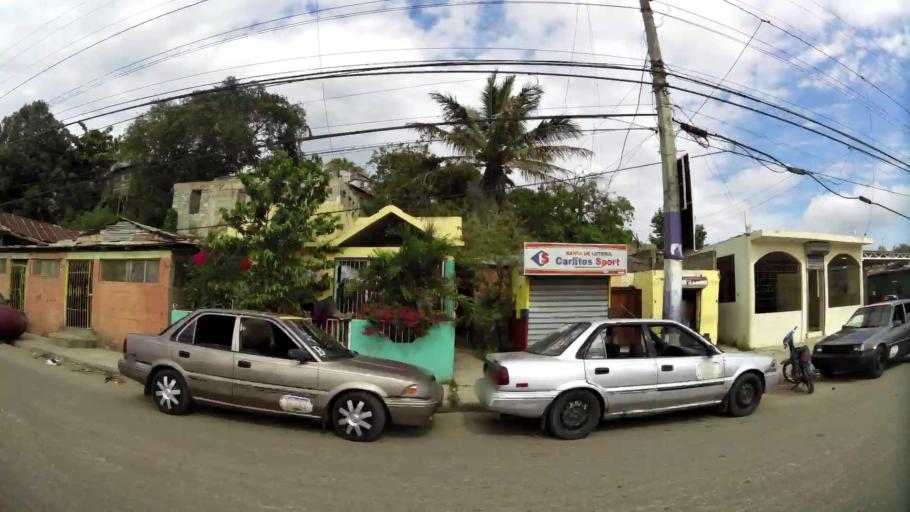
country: DO
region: Santiago
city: Santiago de los Caballeros
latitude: 19.4286
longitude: -70.7089
